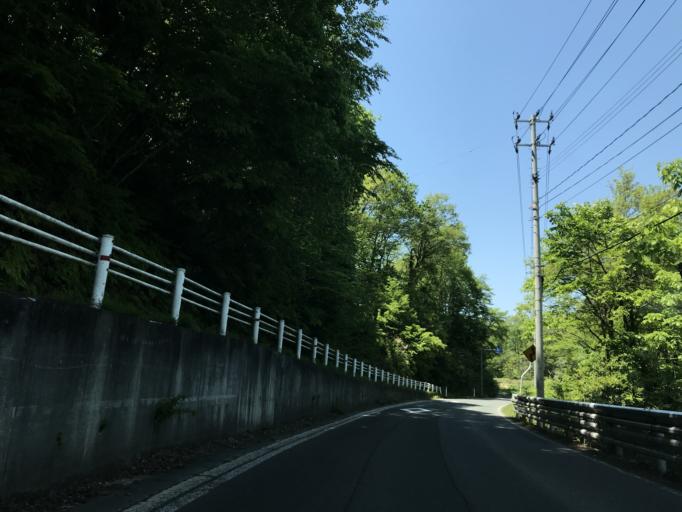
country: JP
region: Akita
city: Yokotemachi
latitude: 39.3566
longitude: 140.7643
